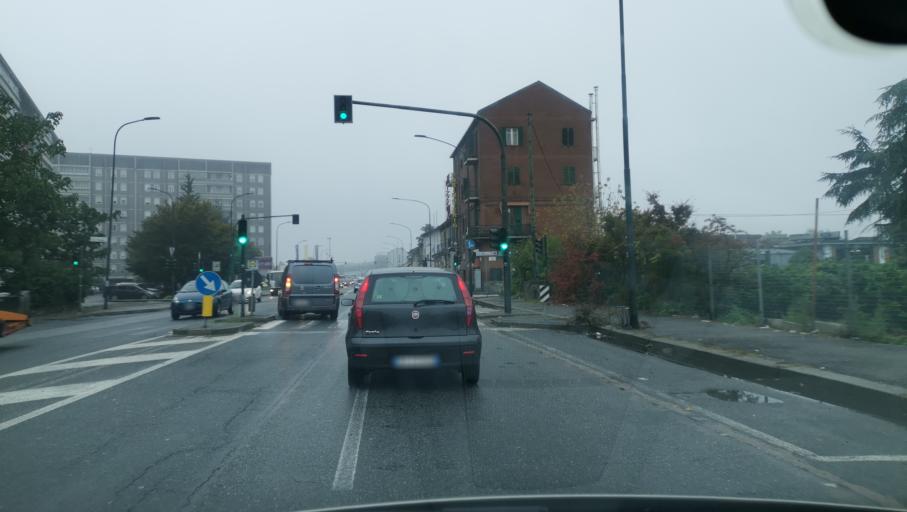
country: IT
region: Piedmont
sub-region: Provincia di Torino
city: Turin
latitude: 45.1080
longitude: 7.6905
